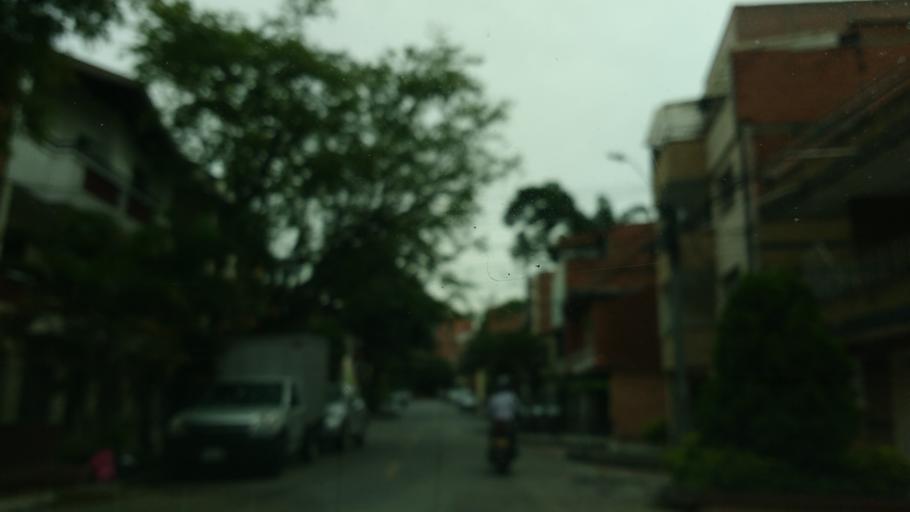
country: CO
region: Antioquia
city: Medellin
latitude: 6.2541
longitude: -75.6039
